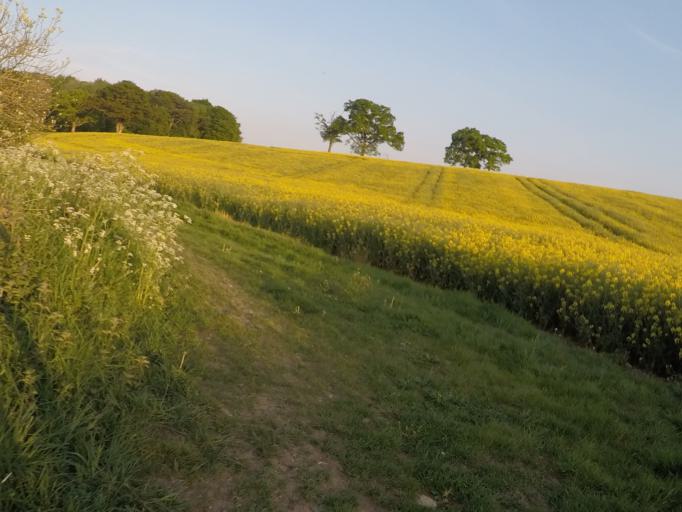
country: GB
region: England
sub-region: Oxfordshire
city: Charlbury
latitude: 51.8447
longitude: -1.5348
